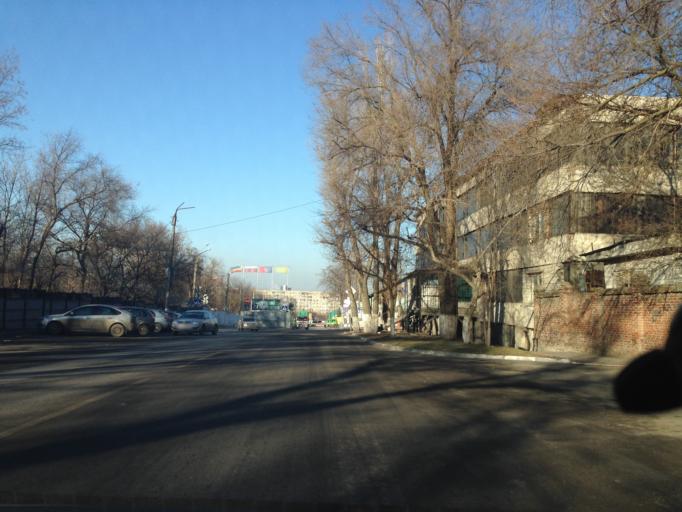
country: RU
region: Rostov
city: Rostov-na-Donu
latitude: 47.2401
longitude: 39.7188
